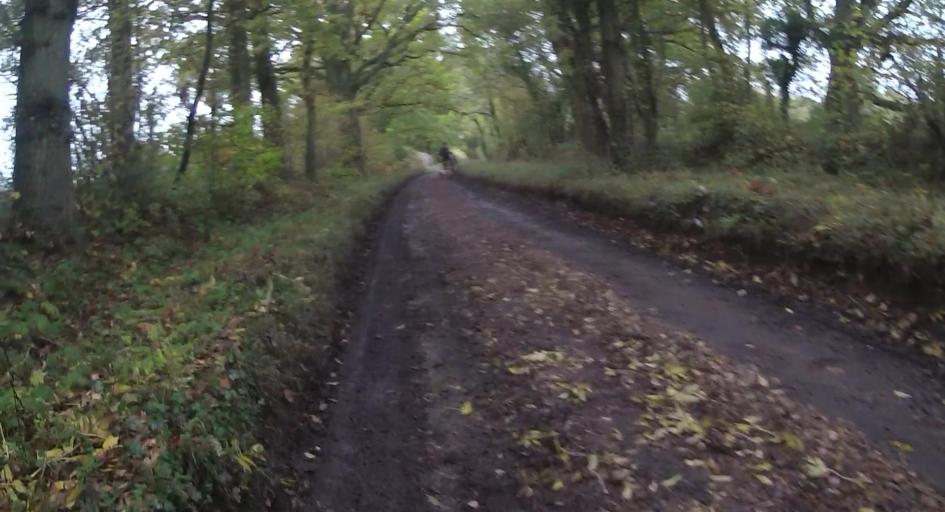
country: GB
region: England
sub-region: Surrey
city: Farnham
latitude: 51.2259
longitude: -0.8168
